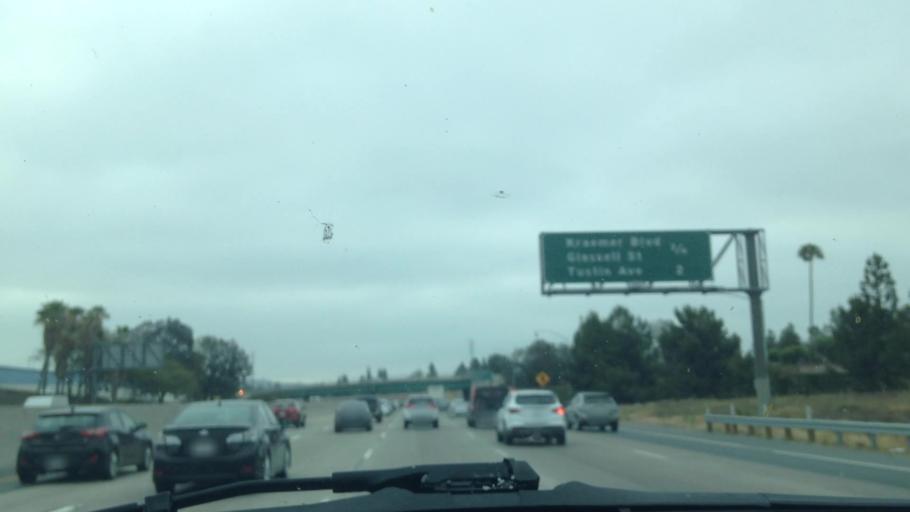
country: US
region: California
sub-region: Orange County
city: Placentia
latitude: 33.8489
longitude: -117.8742
